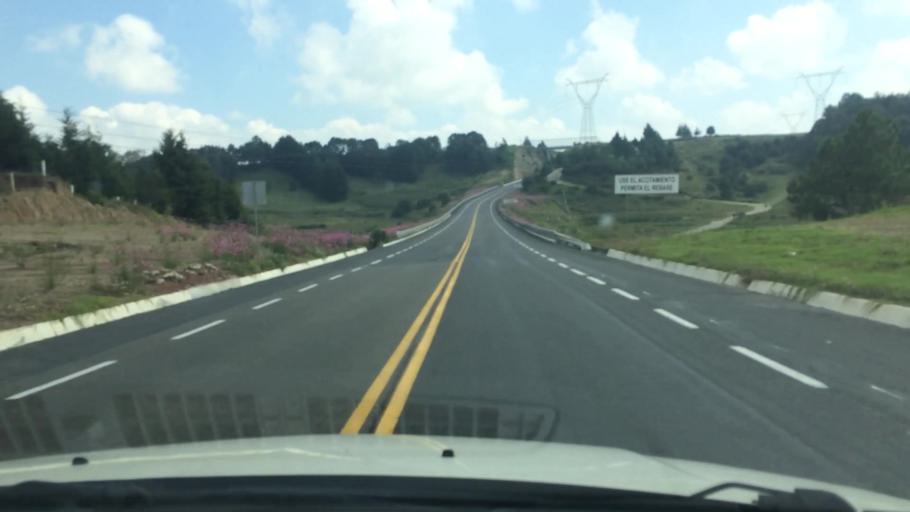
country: MX
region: Mexico
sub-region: Villa Victoria
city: Colonia Doctor Gustavo Baz
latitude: 19.3675
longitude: -99.9407
